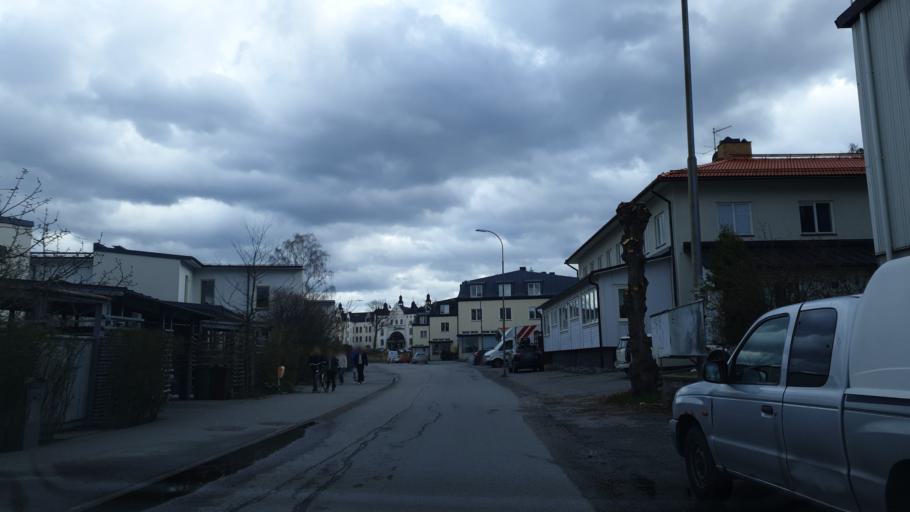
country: SE
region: Stockholm
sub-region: Nacka Kommun
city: Saltsjobaden
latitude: 59.2793
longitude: 18.3083
